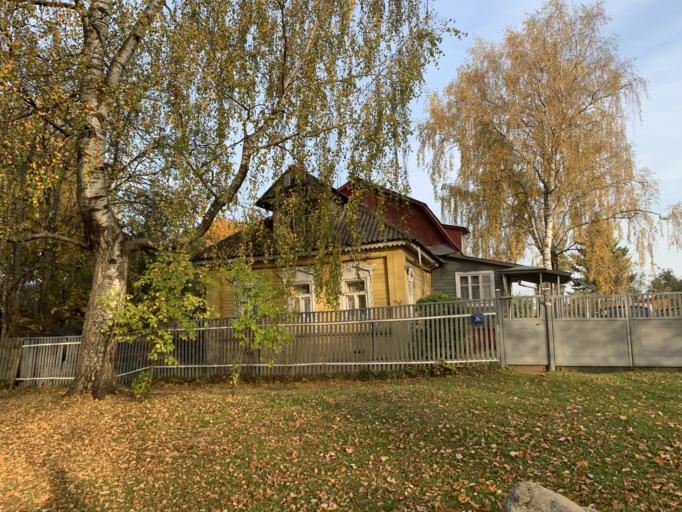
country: RU
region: Jaroslavl
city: Porech'ye-Rybnoye
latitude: 56.9800
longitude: 39.3835
